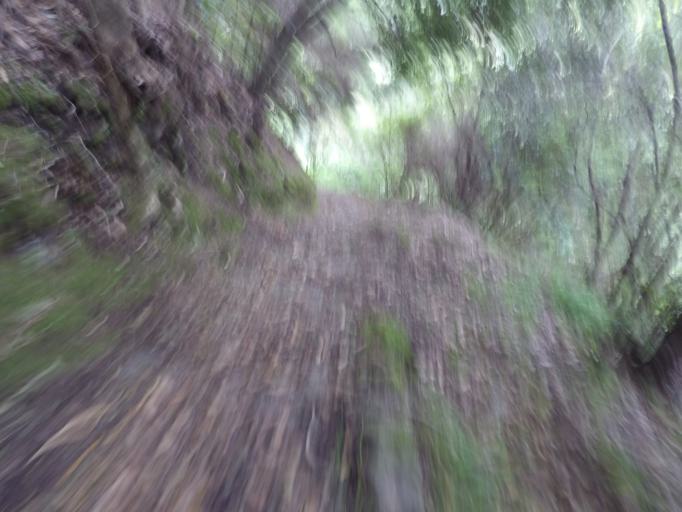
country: PT
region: Madeira
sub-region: Camara de Lobos
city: Curral das Freiras
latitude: 32.7790
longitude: -16.9790
